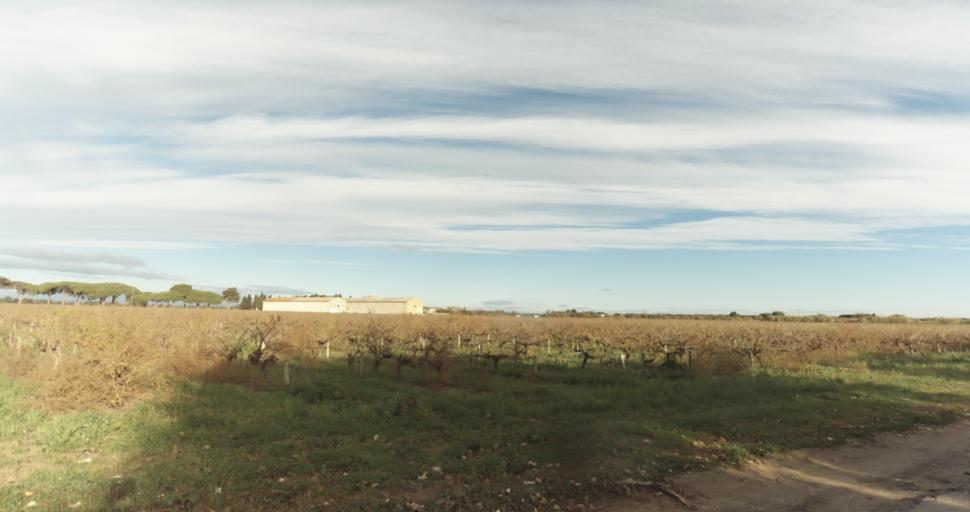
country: FR
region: Languedoc-Roussillon
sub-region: Departement du Gard
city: Aigues-Mortes
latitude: 43.5590
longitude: 4.2204
